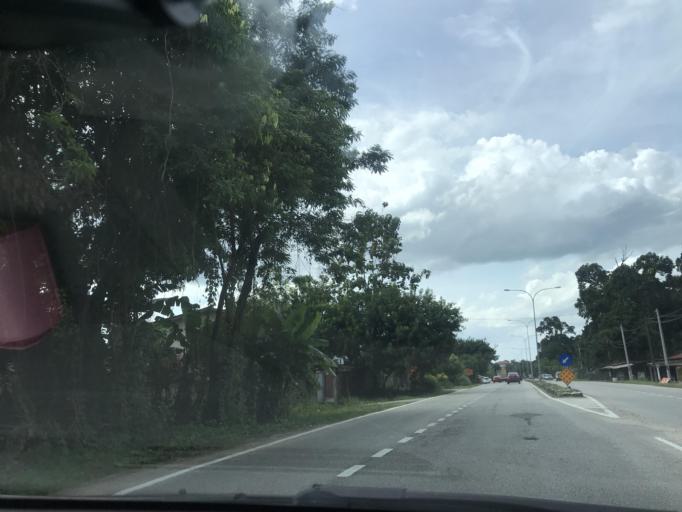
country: MY
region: Kelantan
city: Kampong Pangkal Kalong
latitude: 5.9175
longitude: 102.1883
